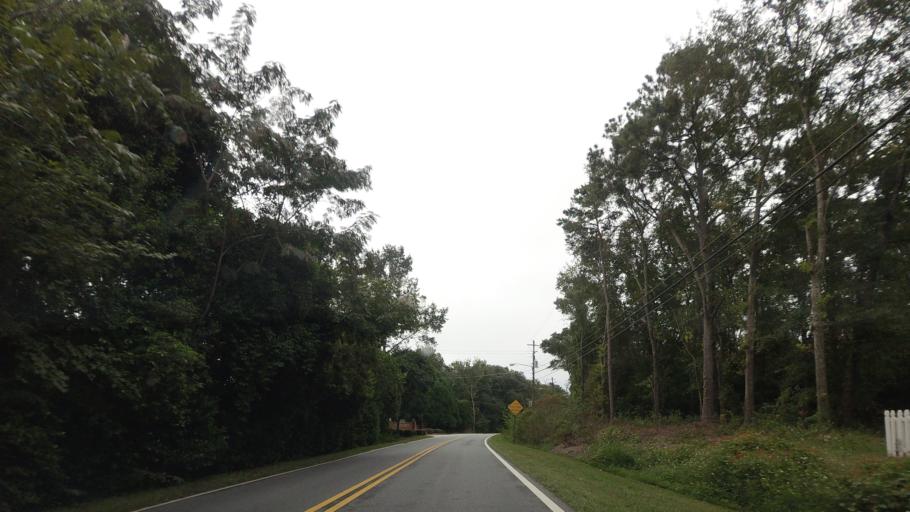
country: US
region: Georgia
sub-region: Lowndes County
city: Remerton
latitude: 30.8834
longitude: -83.3005
